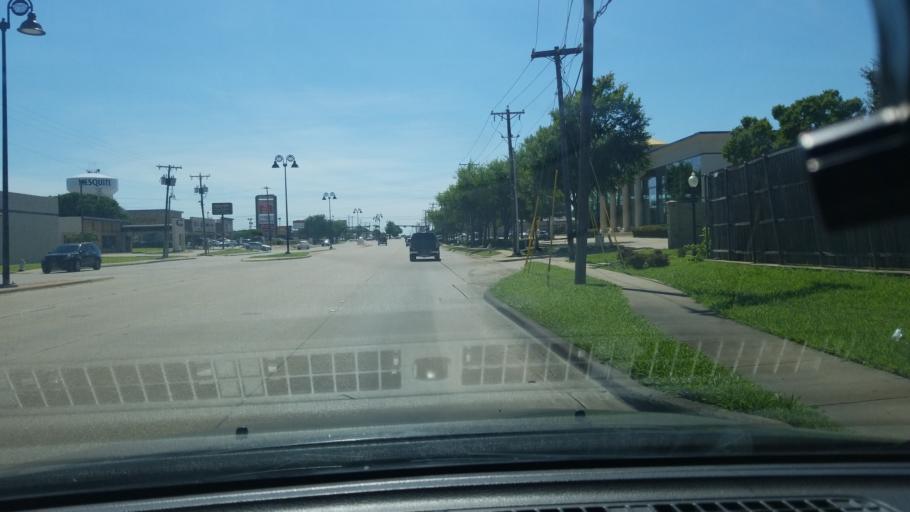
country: US
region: Texas
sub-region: Dallas County
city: Mesquite
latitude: 32.8109
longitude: -96.6132
